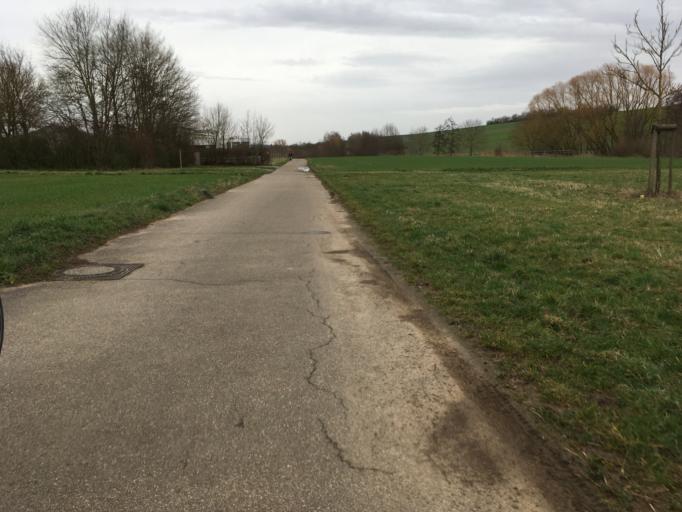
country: DE
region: Baden-Wuerttemberg
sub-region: Regierungsbezirk Stuttgart
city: Nordheim
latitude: 49.1022
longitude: 9.1190
